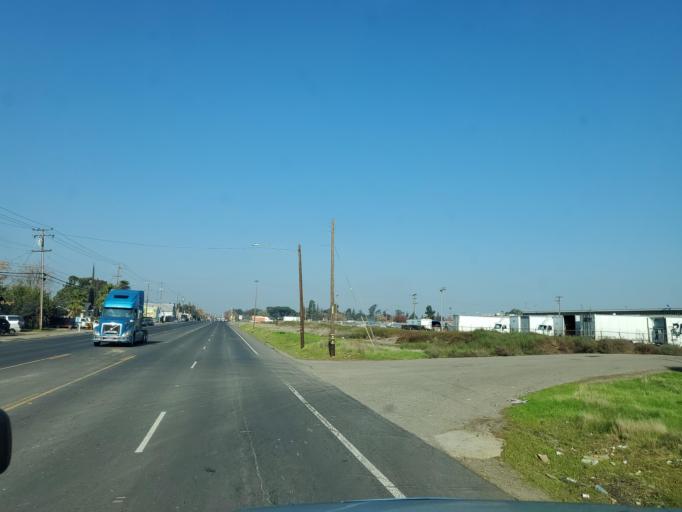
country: US
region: California
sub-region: San Joaquin County
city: Taft Mosswood
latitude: 37.9209
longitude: -121.2795
